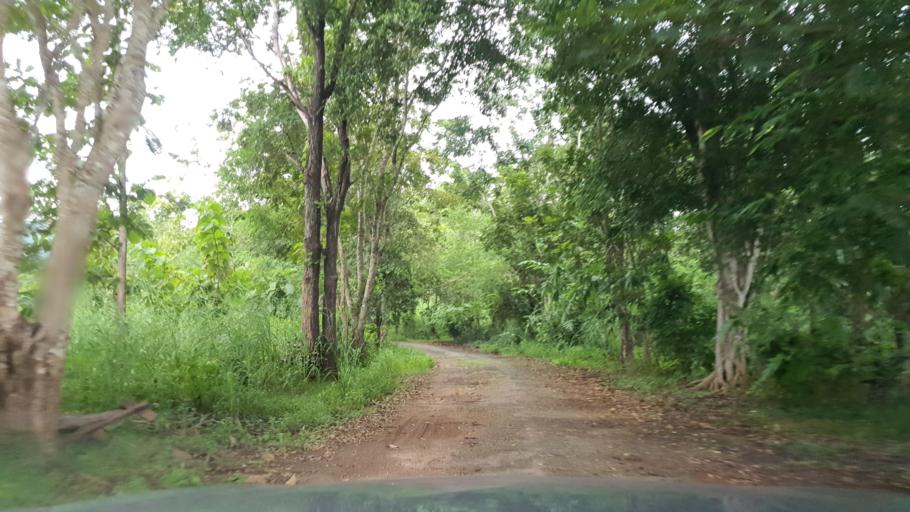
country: TH
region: Chiang Mai
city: Mae Taeng
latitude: 19.2280
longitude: 98.9716
